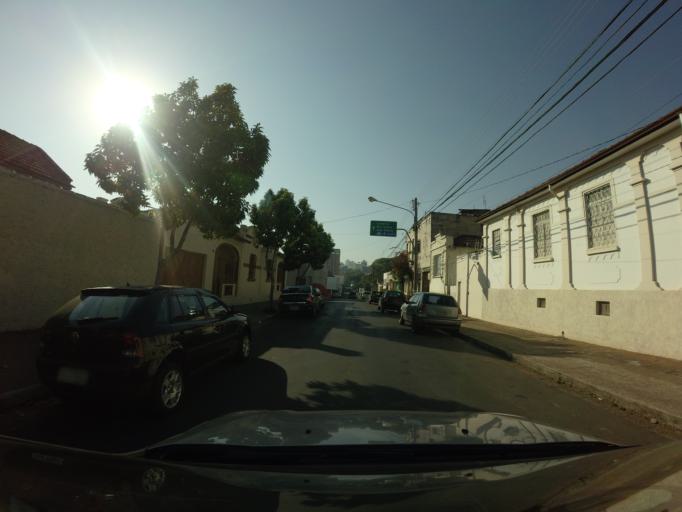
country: BR
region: Sao Paulo
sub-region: Piracicaba
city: Piracicaba
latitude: -22.7333
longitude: -47.6504
